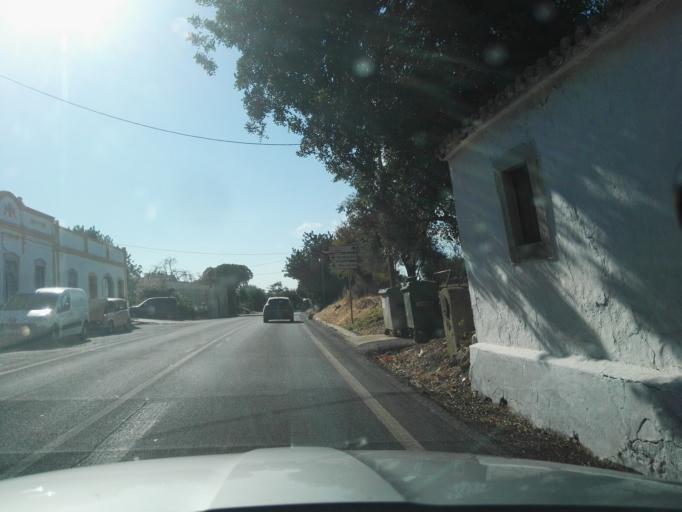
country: PT
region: Faro
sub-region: Sao Bras de Alportel
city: Sao Bras de Alportel
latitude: 37.1550
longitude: -7.8465
